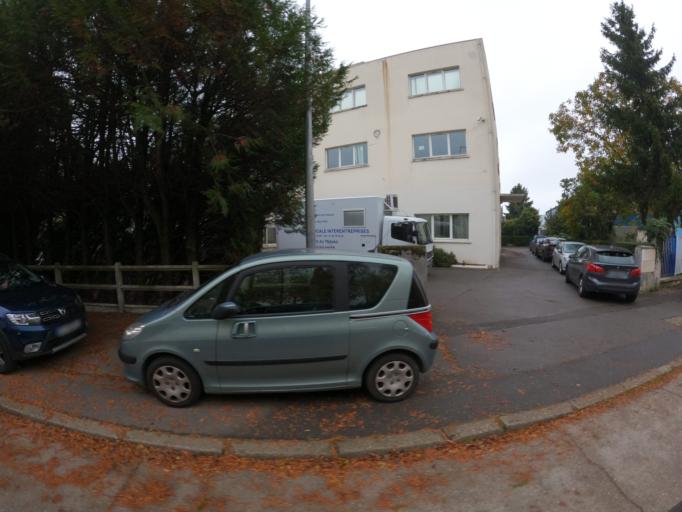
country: FR
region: Ile-de-France
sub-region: Departement du Val-de-Marne
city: Ormesson-sur-Marne
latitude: 48.7933
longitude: 2.5468
